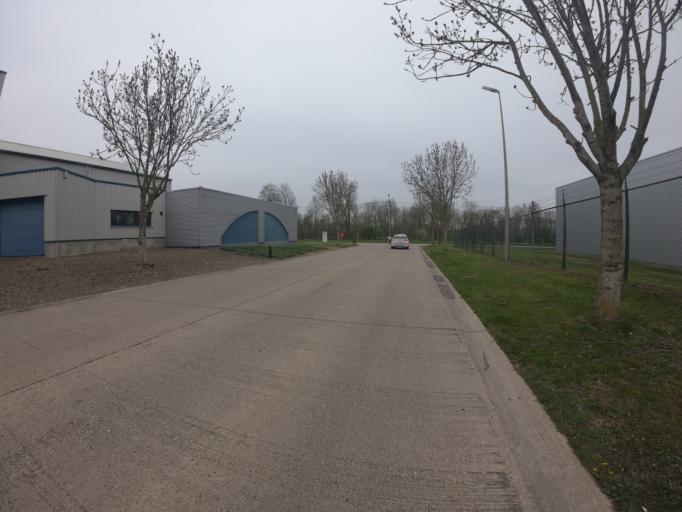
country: BE
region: Flanders
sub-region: Provincie Limburg
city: Lanaken
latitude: 50.8908
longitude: 5.6674
